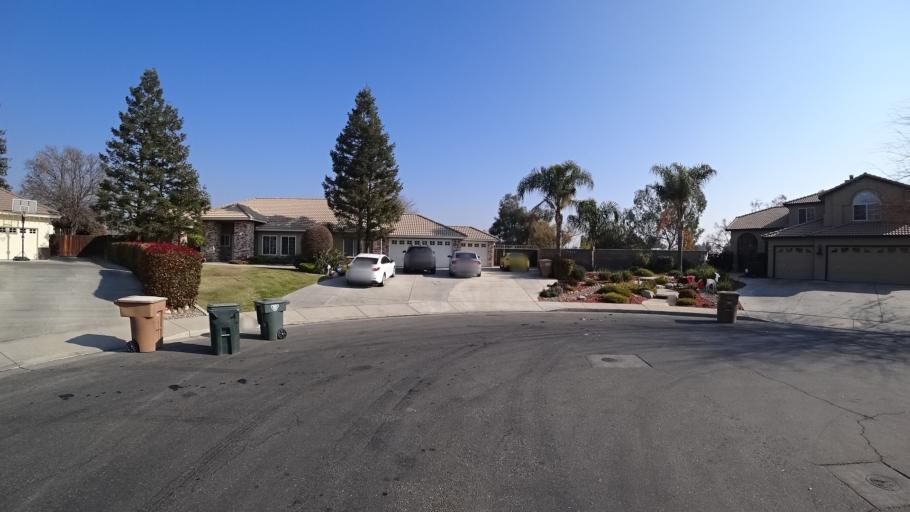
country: US
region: California
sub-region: Kern County
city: Oildale
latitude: 35.4083
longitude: -118.8682
